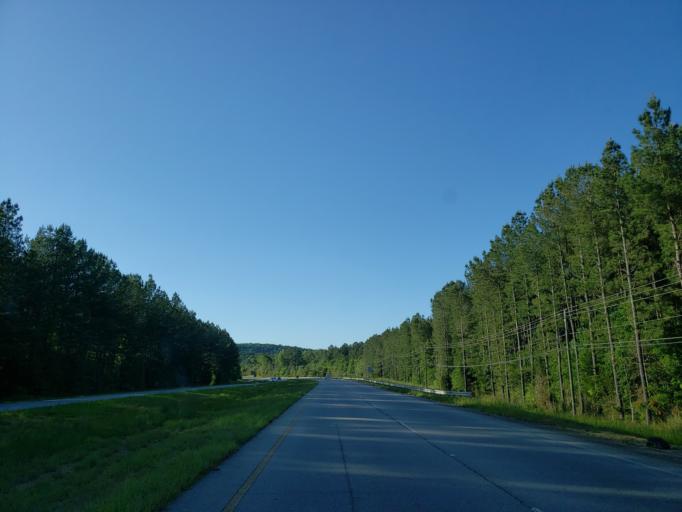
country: US
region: Georgia
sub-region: Polk County
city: Cedartown
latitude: 33.9491
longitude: -85.2442
